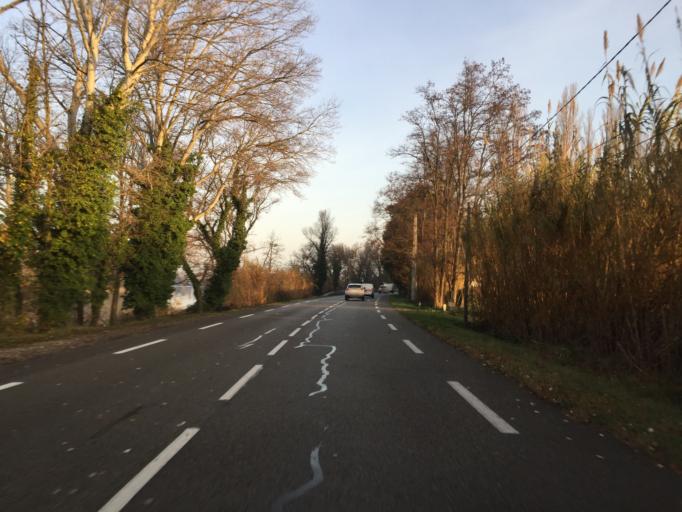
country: FR
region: Languedoc-Roussillon
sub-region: Departement du Gard
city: Montfaucon
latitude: 44.0817
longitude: 4.7611
